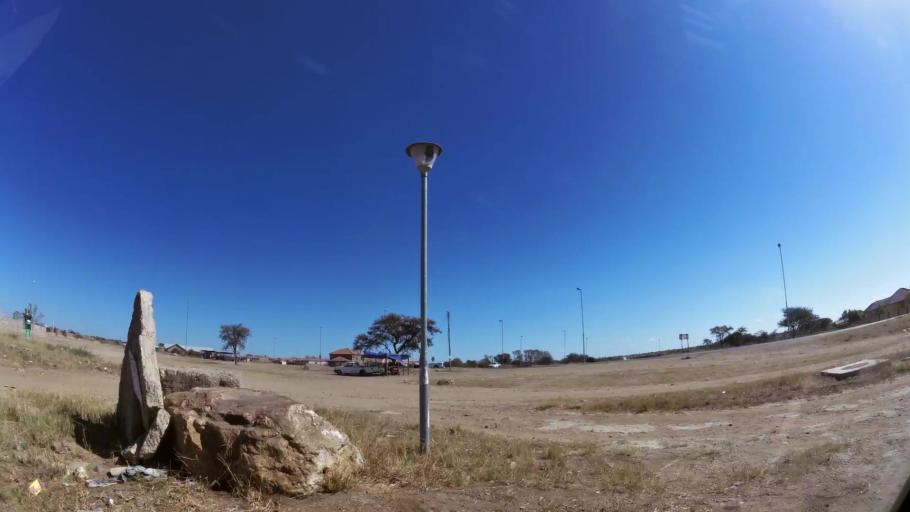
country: ZA
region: Limpopo
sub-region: Capricorn District Municipality
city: Polokwane
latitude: -23.8695
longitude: 29.4262
